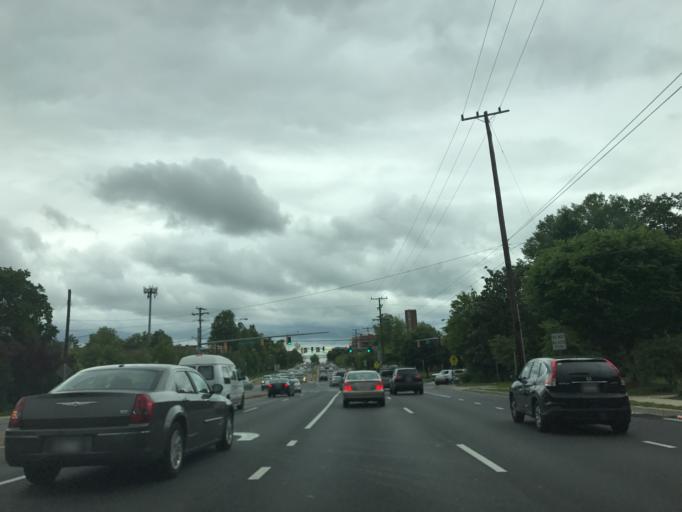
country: US
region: Maryland
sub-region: Prince George's County
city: University Park
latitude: 38.9663
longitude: -76.9474
